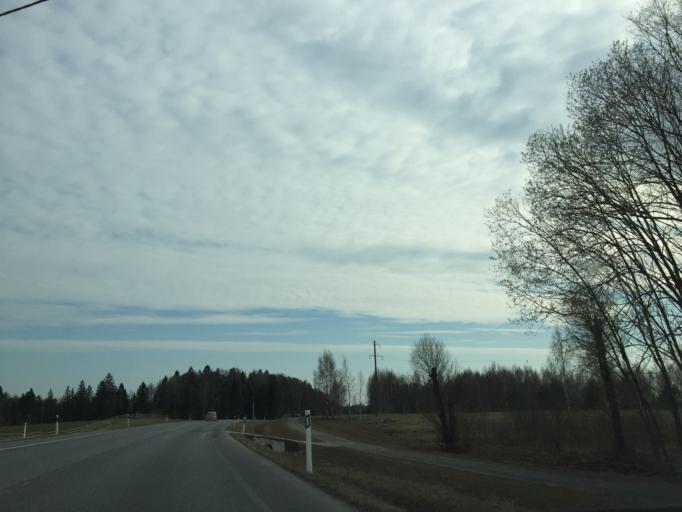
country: EE
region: Ida-Virumaa
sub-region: Johvi vald
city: Johvi
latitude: 59.2494
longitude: 27.5206
